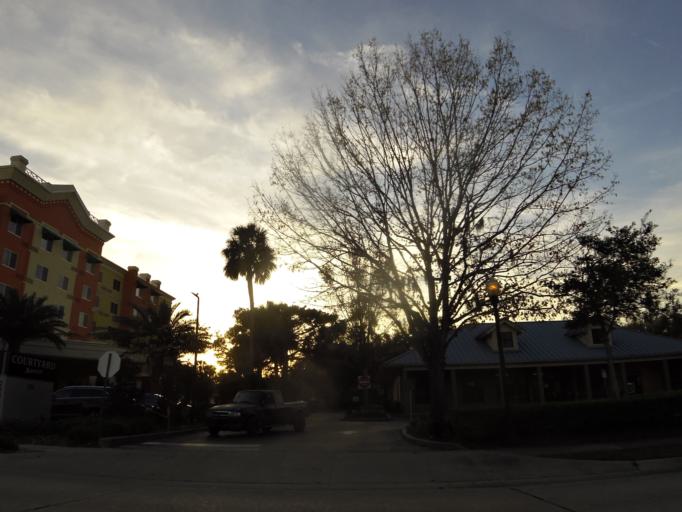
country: US
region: Florida
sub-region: Volusia County
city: DeLand
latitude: 29.0323
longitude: -81.3036
